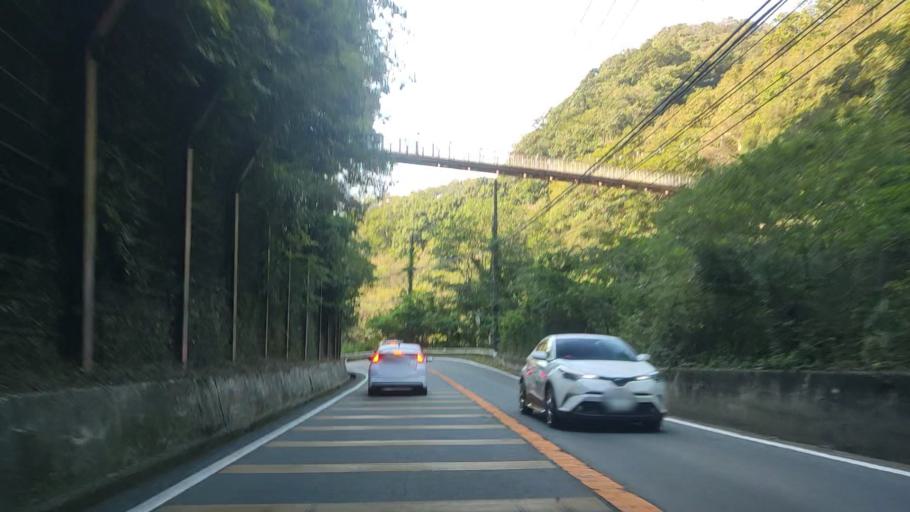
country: JP
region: Hyogo
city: Kobe
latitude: 34.7156
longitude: 135.1595
